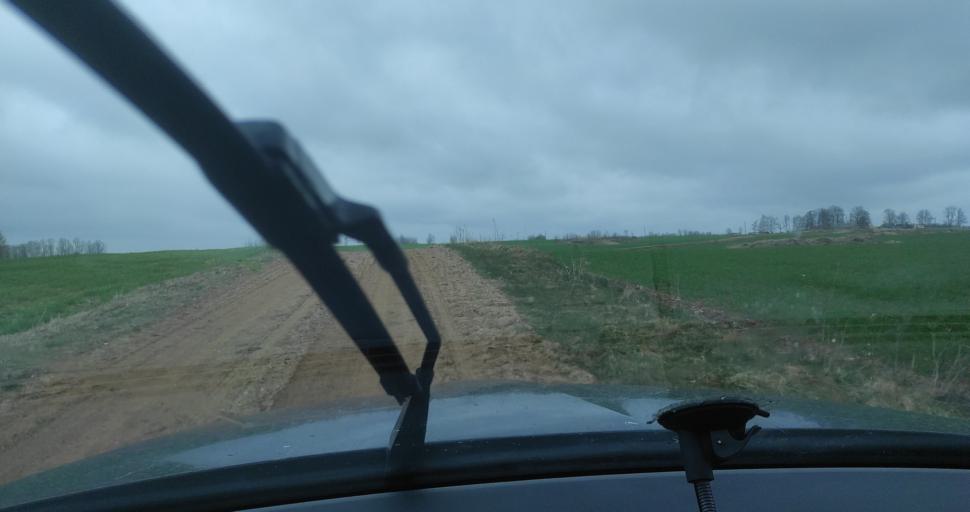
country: LV
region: Broceni
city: Broceni
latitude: 56.7419
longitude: 22.4859
